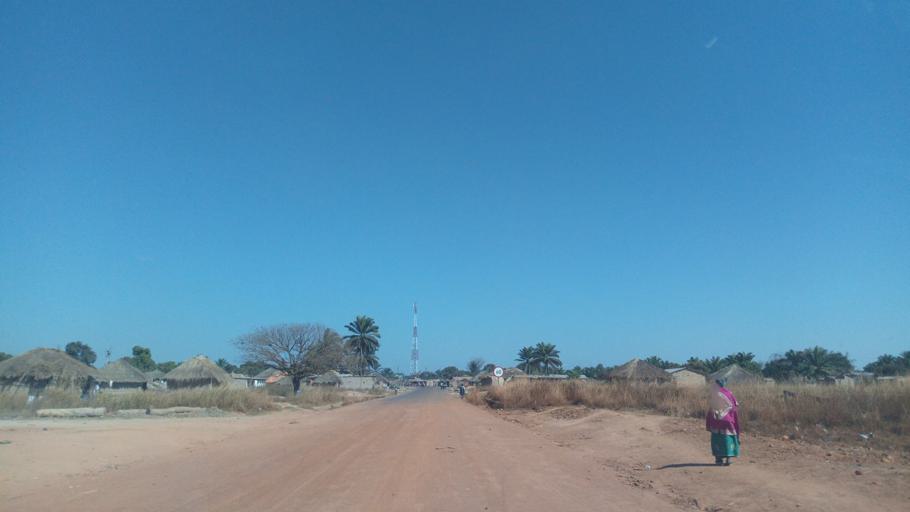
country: ZM
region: Luapula
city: Mwense
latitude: -10.7556
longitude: 28.2871
